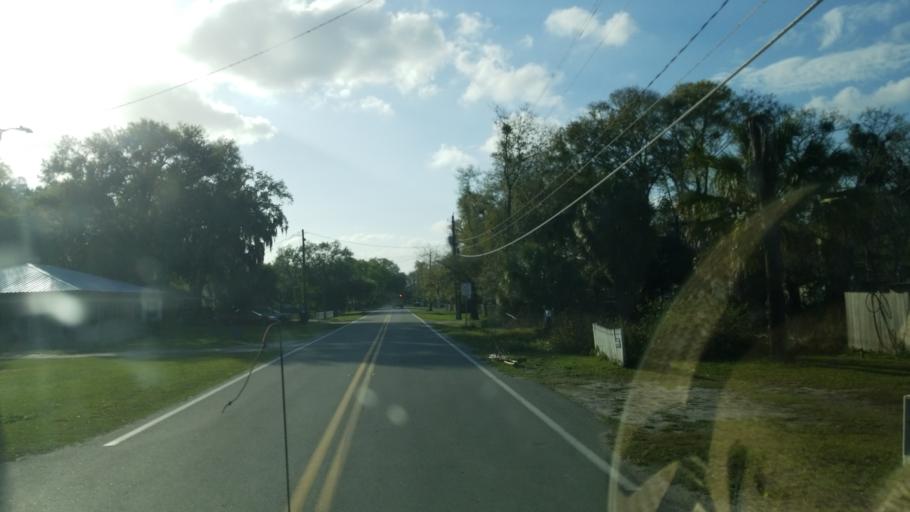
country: US
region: Florida
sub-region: Polk County
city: Mulberry
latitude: 27.7941
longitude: -81.9787
